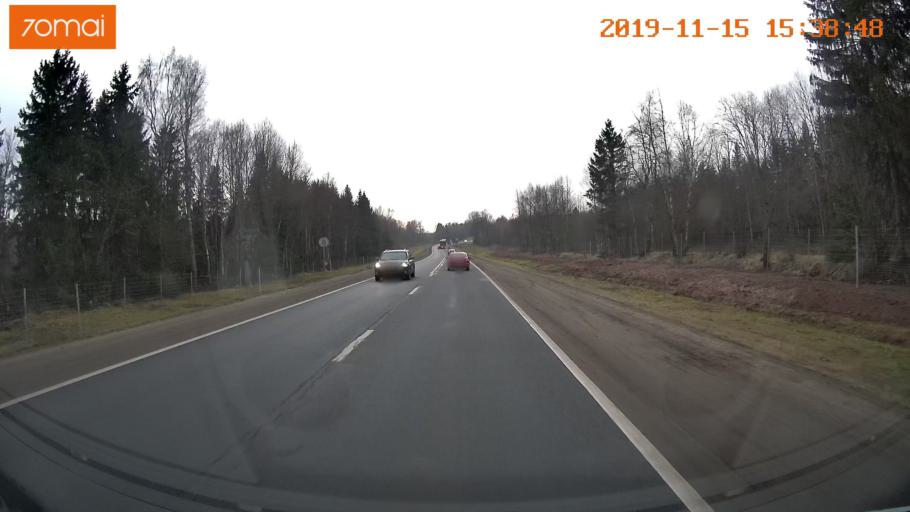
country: RU
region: Jaroslavl
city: Danilov
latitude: 58.0266
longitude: 40.0761
